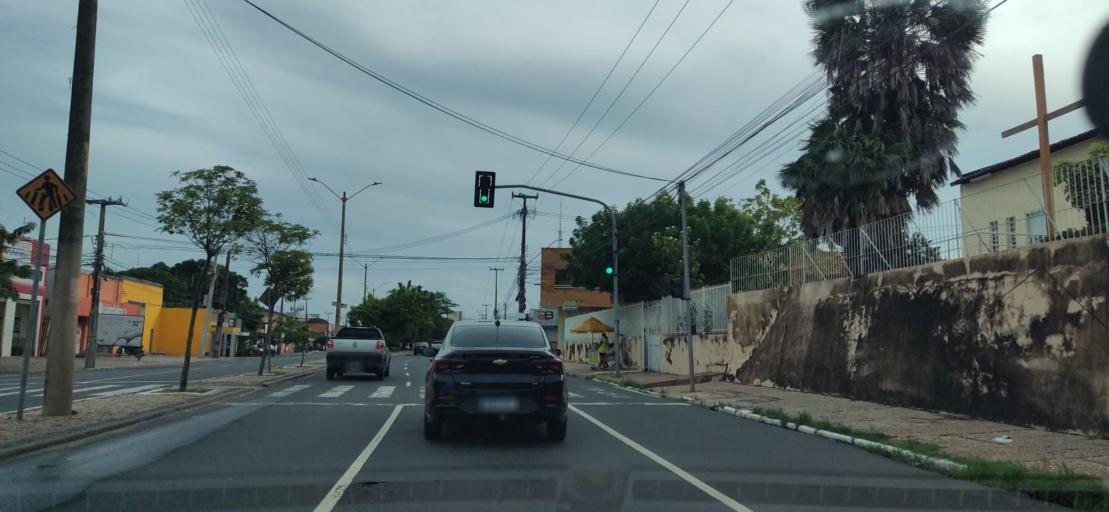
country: BR
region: Piaui
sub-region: Teresina
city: Teresina
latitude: -5.1074
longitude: -42.7925
